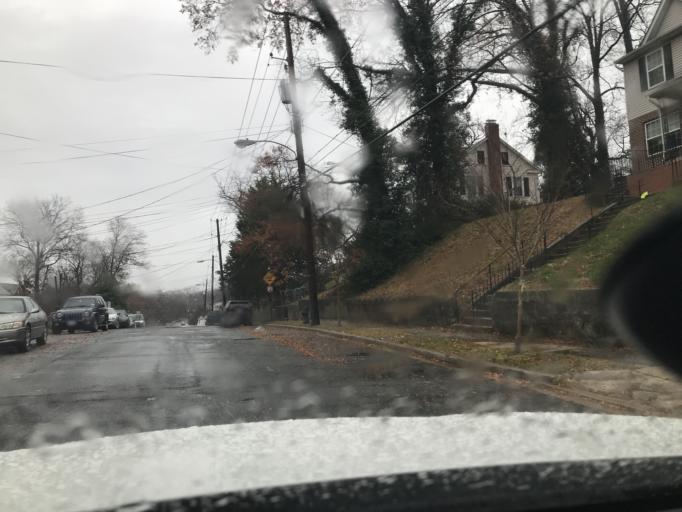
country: US
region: Maryland
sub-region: Prince George's County
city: Fairmount Heights
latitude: 38.8984
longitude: -76.9413
